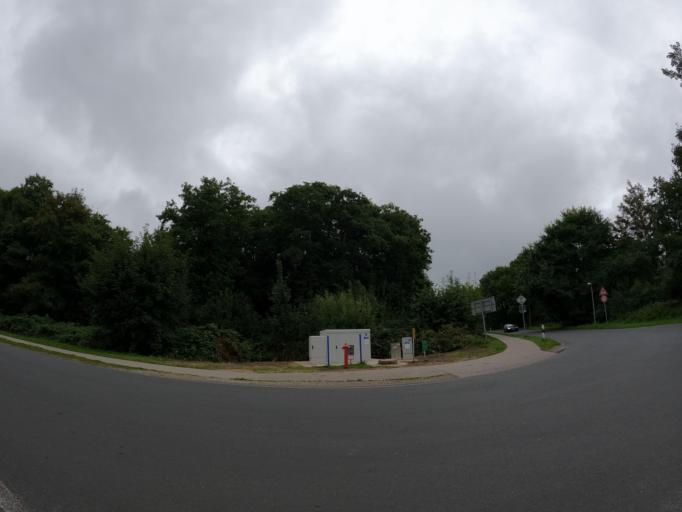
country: DE
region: Mecklenburg-Vorpommern
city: Ostseebad Gohren
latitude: 54.3026
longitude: 13.7023
